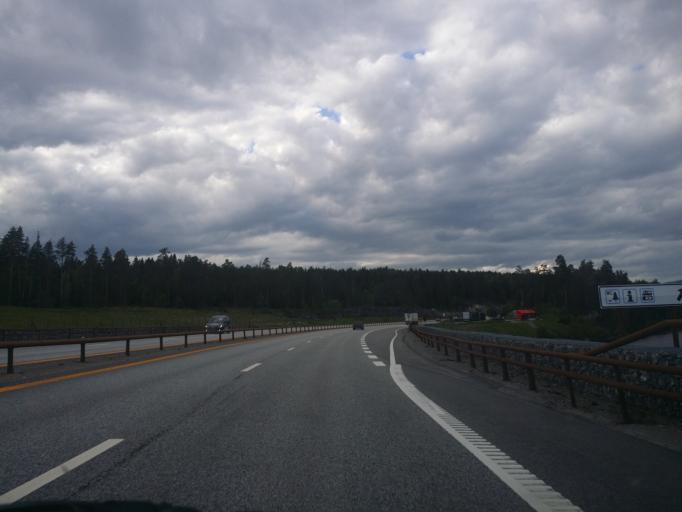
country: NO
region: Akershus
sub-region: Eidsvoll
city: Raholt
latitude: 60.2864
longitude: 11.1349
